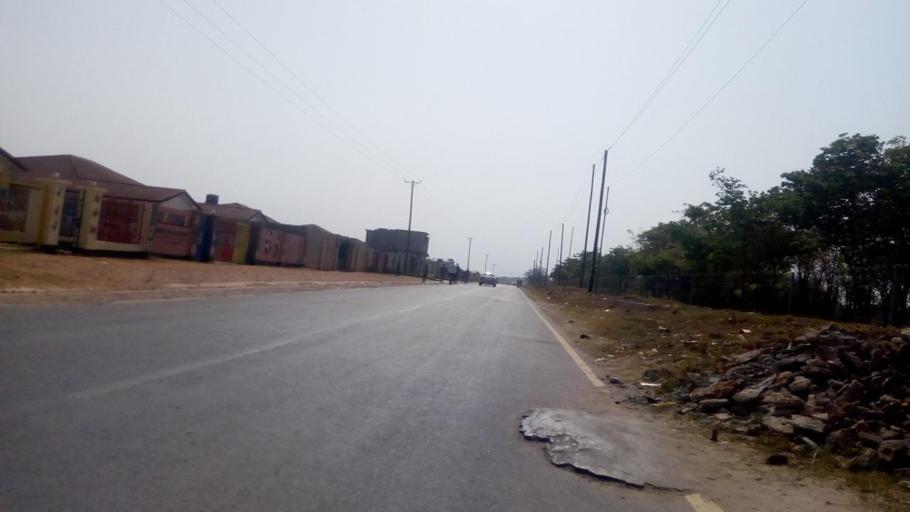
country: ZM
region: Lusaka
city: Lusaka
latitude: -15.3626
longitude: 28.2792
